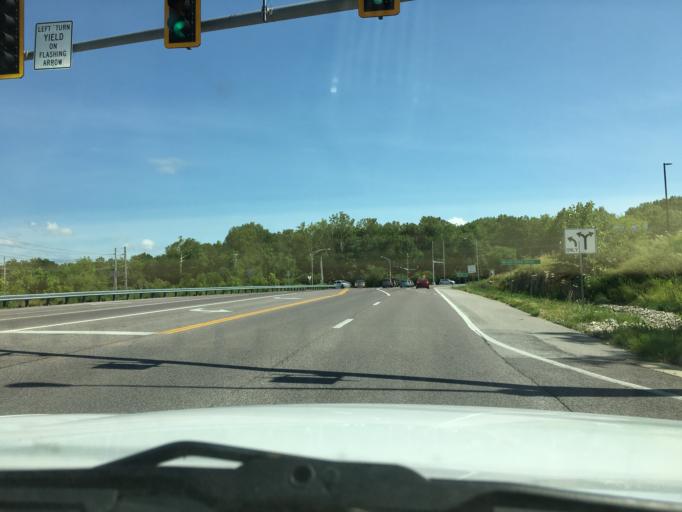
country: US
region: Missouri
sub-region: Franklin County
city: Union
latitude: 38.4457
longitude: -90.9984
